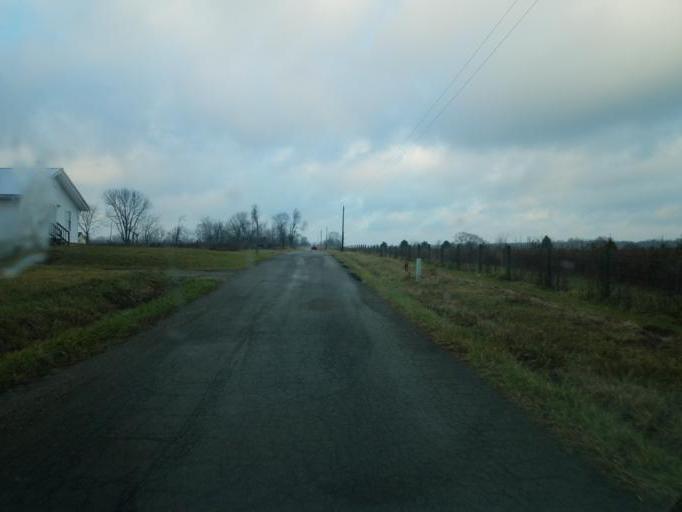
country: US
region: Ohio
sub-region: Knox County
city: Centerburg
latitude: 40.2890
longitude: -82.5729
